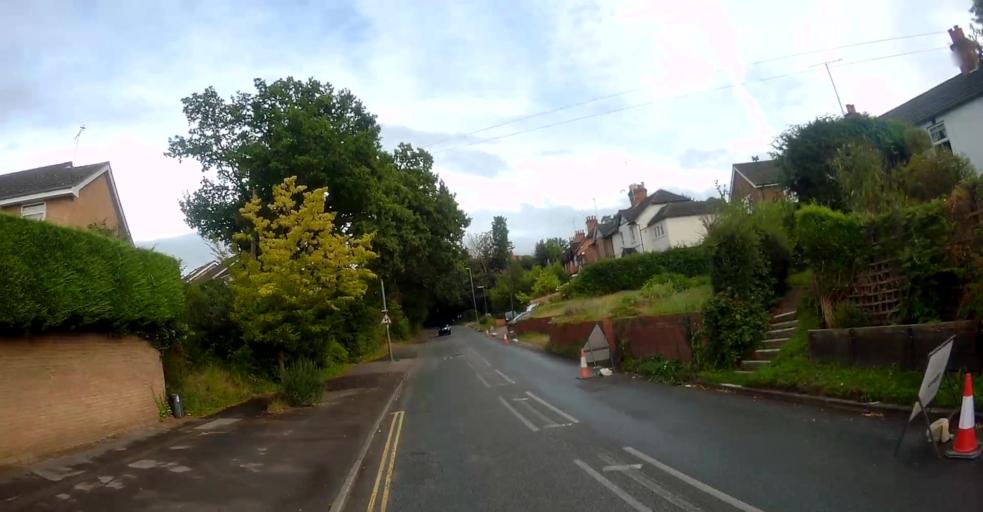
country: GB
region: England
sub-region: Surrey
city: Woking
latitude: 51.3138
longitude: -0.5838
